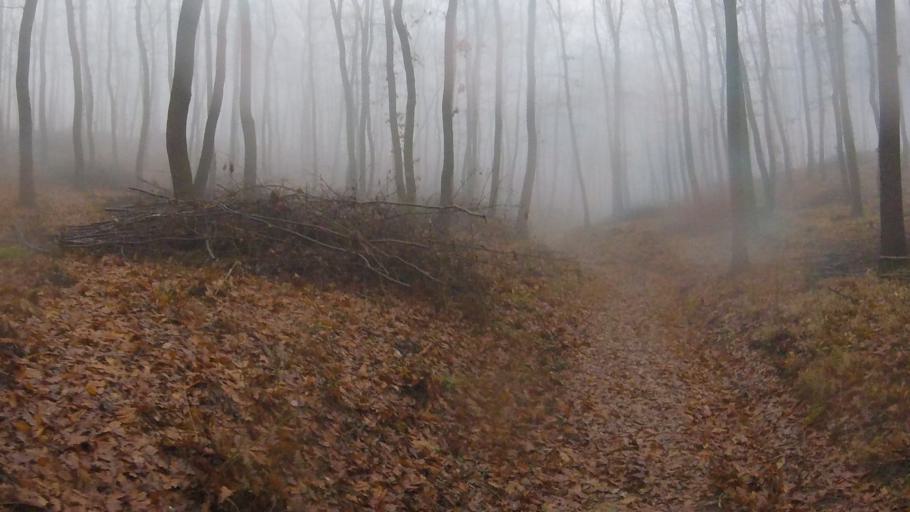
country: HU
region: Pest
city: Biatorbagy
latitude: 47.4522
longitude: 18.8535
